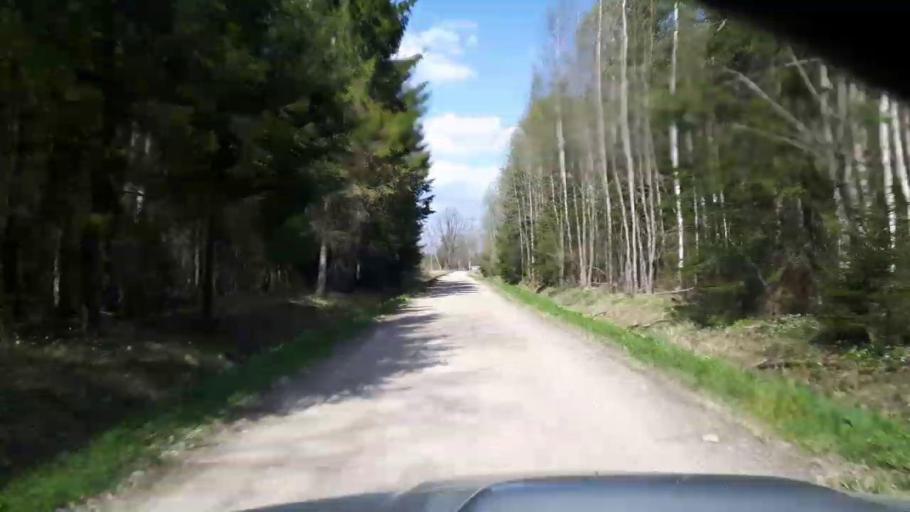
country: EE
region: Paernumaa
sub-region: Tootsi vald
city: Tootsi
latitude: 58.4566
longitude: 24.8868
